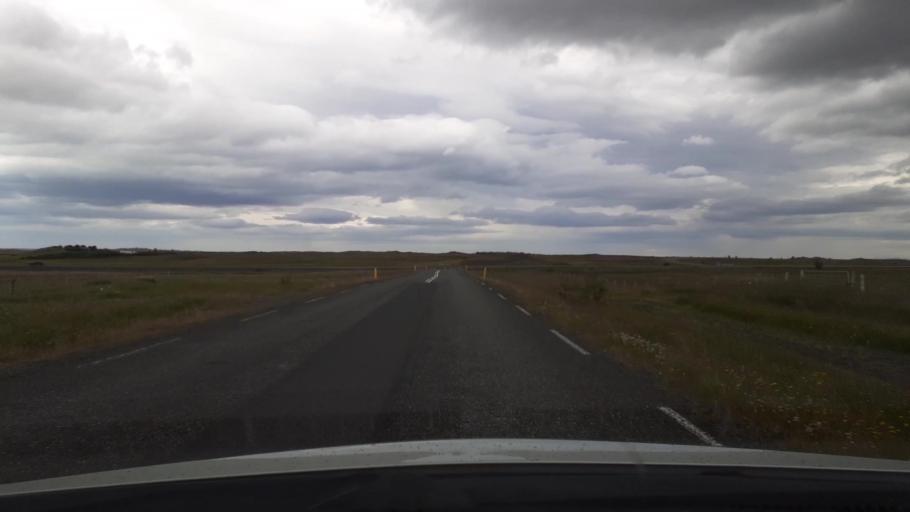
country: IS
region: West
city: Borgarnes
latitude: 64.5550
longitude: -21.7258
